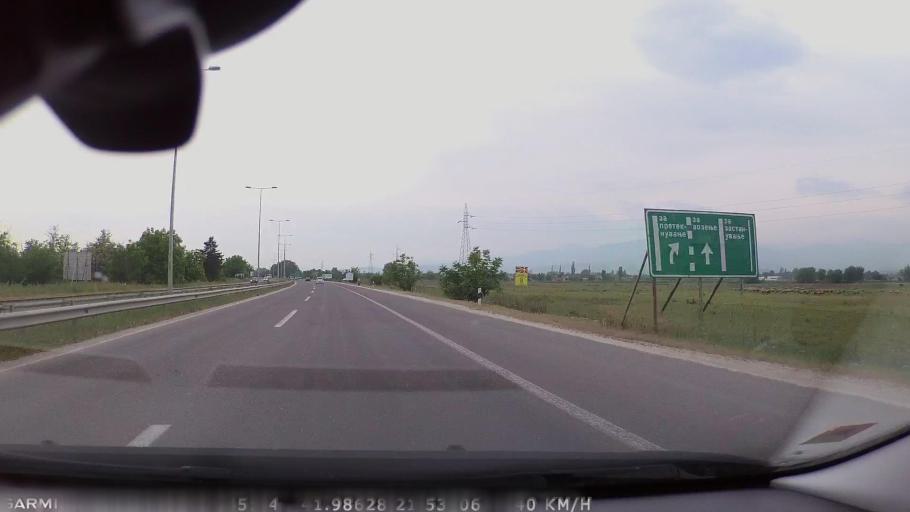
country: MK
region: Ilinden
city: Jurumleri
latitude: 41.9848
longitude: 21.5379
